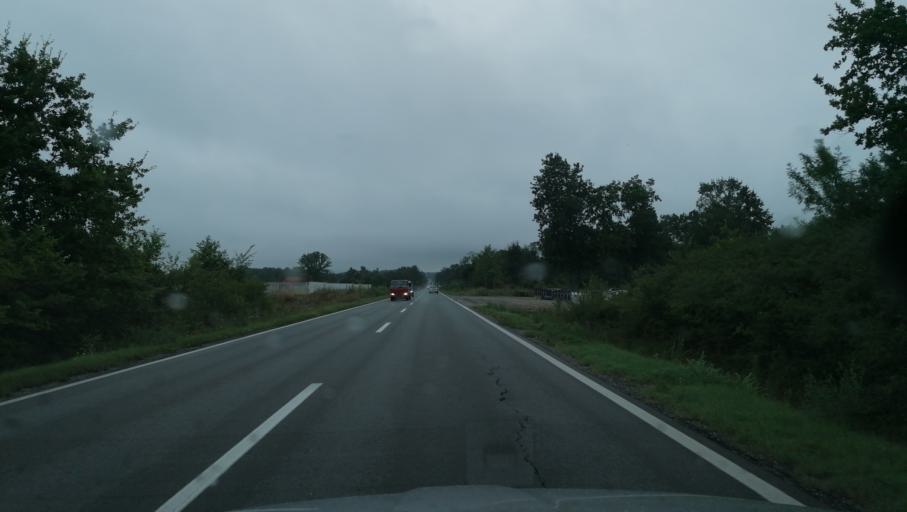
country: RS
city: Prislonica
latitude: 43.8480
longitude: 20.5627
